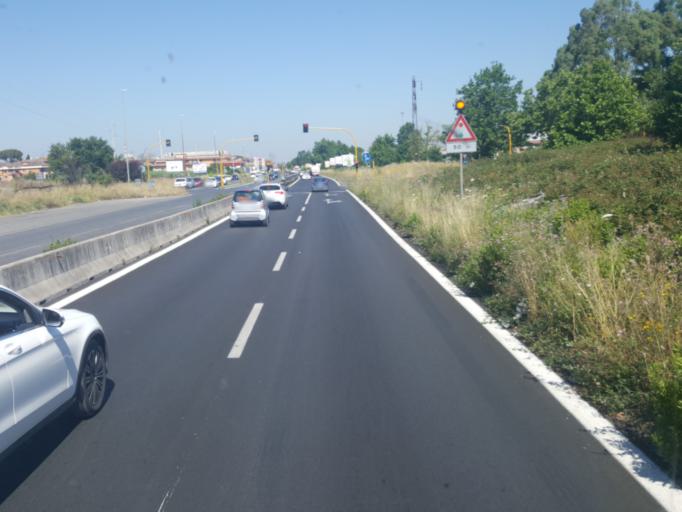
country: IT
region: Latium
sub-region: Citta metropolitana di Roma Capitale
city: Ciampino
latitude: 41.8340
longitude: 12.6075
